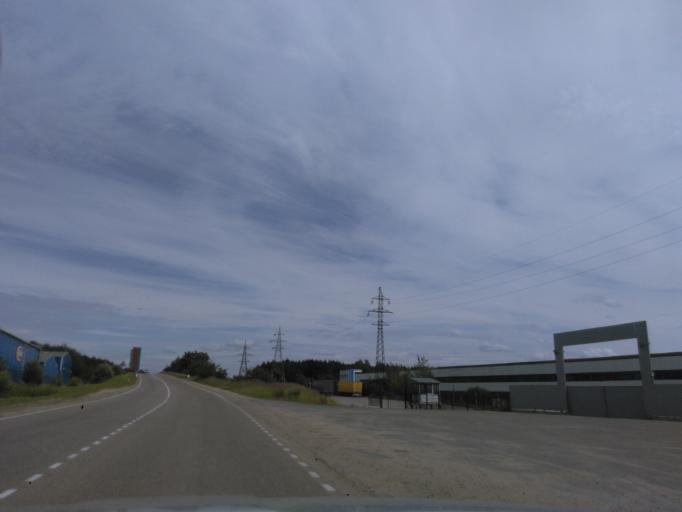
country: RU
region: Moskovskaya
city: Solnechnogorsk
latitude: 56.1639
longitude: 36.9898
